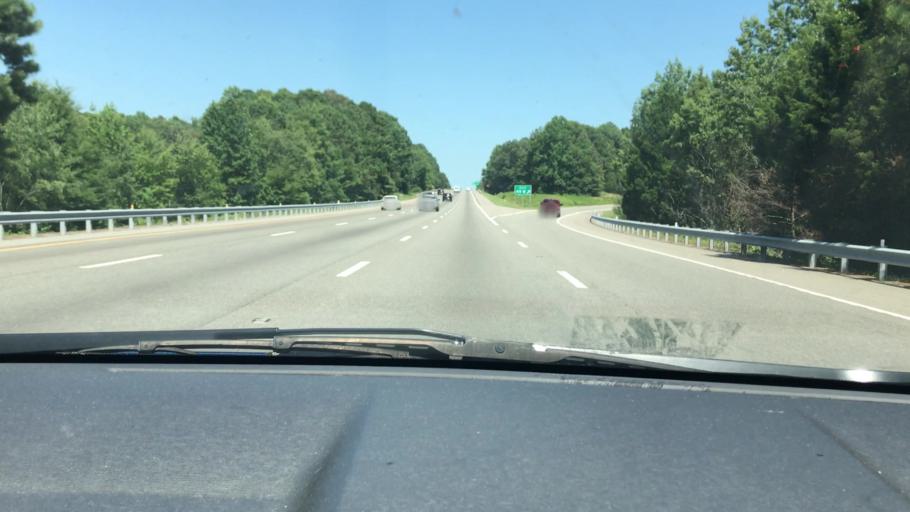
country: US
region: Virginia
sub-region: Henrico County
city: Glen Allen
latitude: 37.6792
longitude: -77.5469
